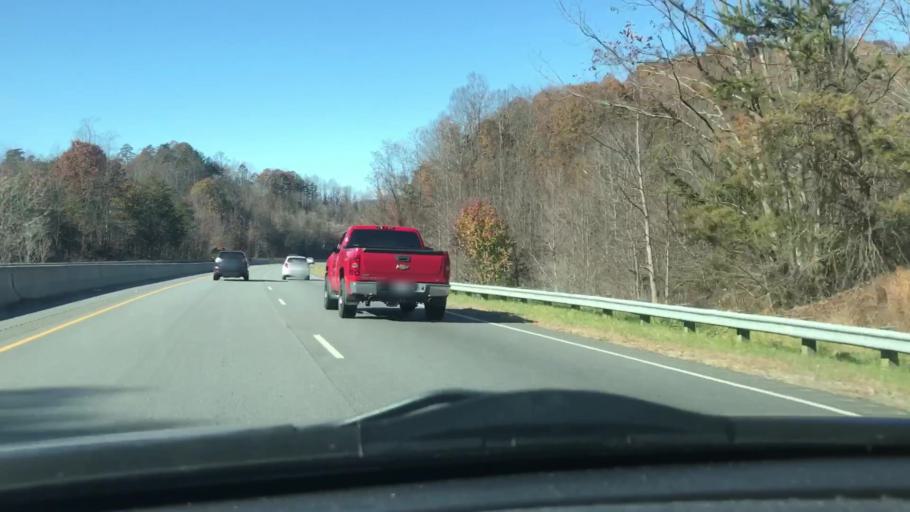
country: US
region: North Carolina
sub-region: McDowell County
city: Marion
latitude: 35.6657
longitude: -82.0060
